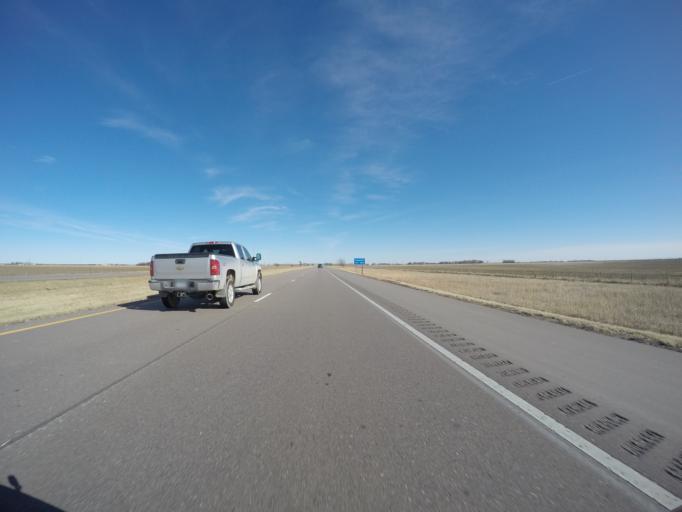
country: US
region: Nebraska
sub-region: York County
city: York
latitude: 40.8212
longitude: -97.6302
